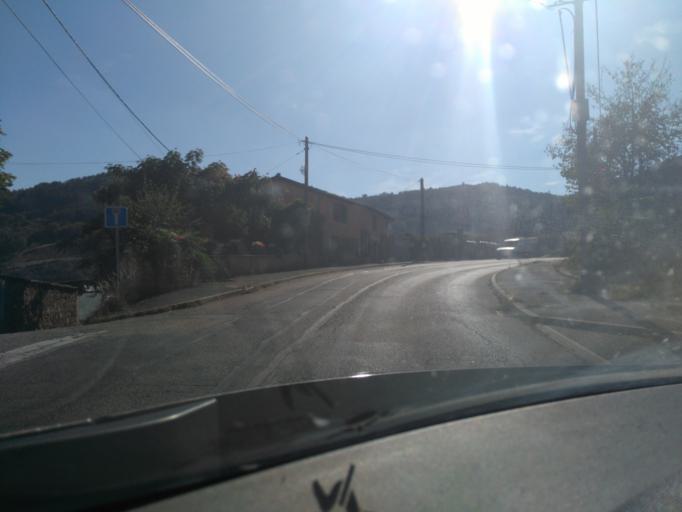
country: FR
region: Rhone-Alpes
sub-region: Departement du Rhone
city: Tarare
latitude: 45.8867
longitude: 4.4349
